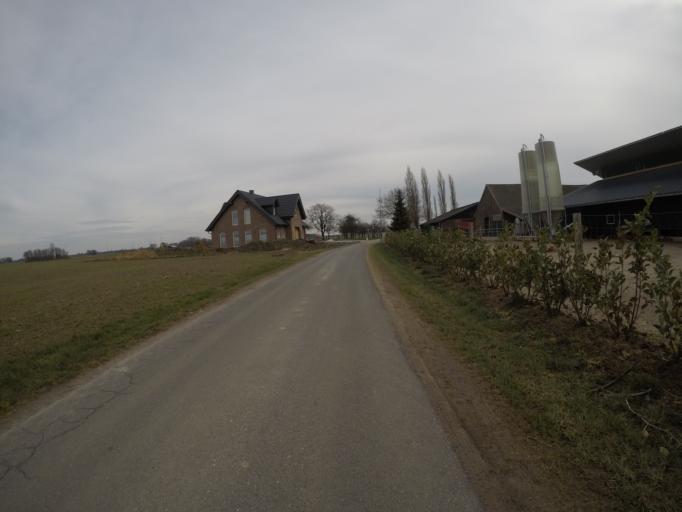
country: DE
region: North Rhine-Westphalia
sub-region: Regierungsbezirk Dusseldorf
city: Mehrhoog
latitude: 51.7899
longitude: 6.5413
